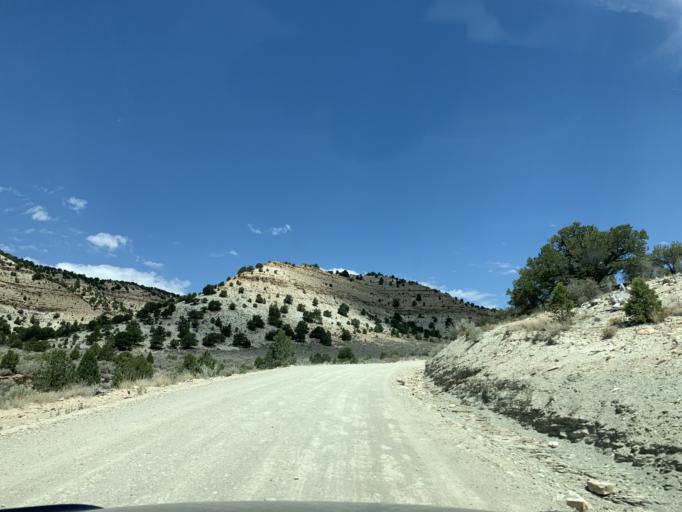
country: US
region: Utah
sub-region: Duchesne County
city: Duchesne
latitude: 39.8670
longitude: -110.2494
